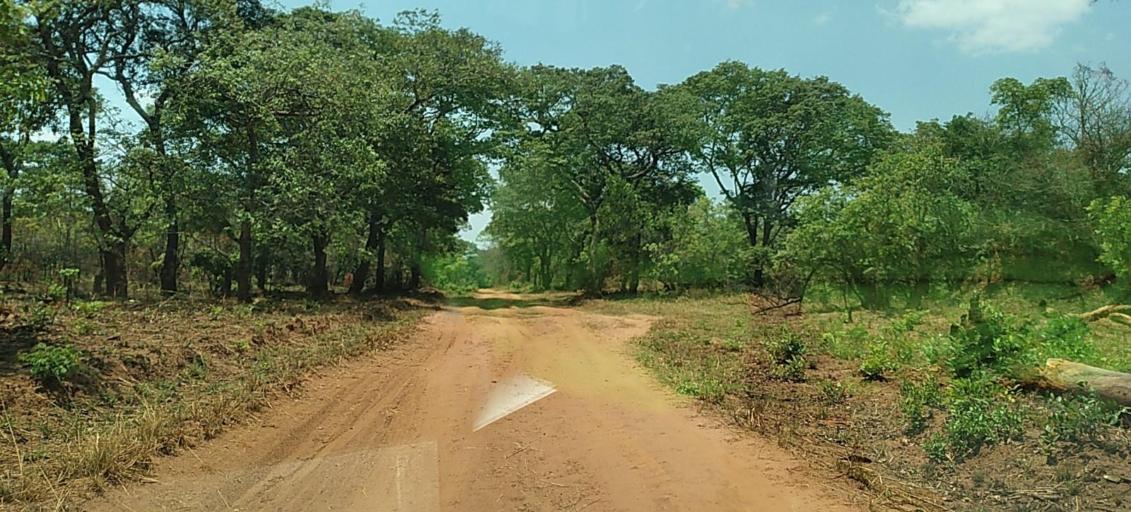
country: CD
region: Katanga
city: Kolwezi
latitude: -11.3563
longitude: 25.2094
